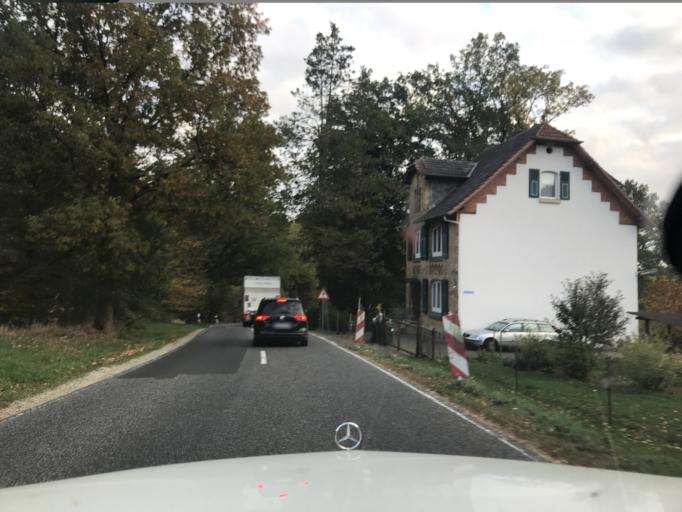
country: DE
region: Hesse
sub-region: Regierungsbezirk Kassel
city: Fuldatal
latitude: 51.4123
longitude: 9.5469
